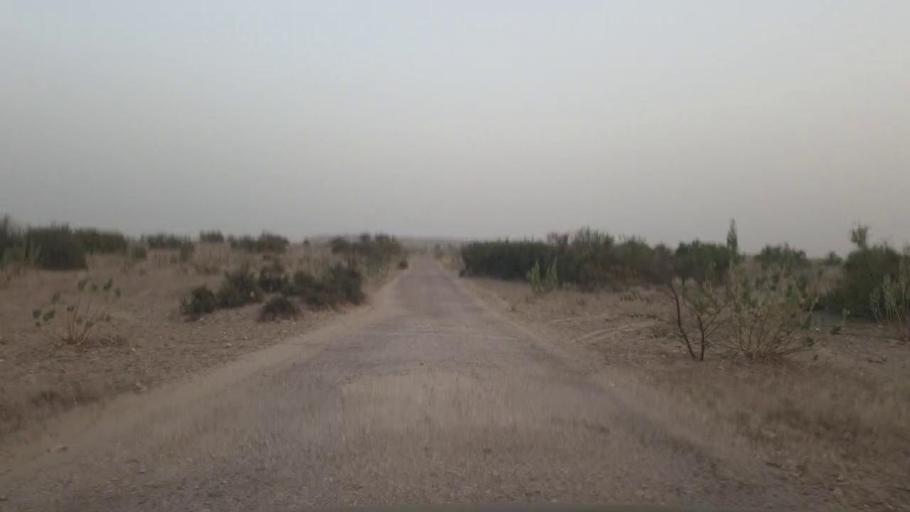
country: PK
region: Sindh
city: Chor
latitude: 25.5065
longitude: 69.8188
